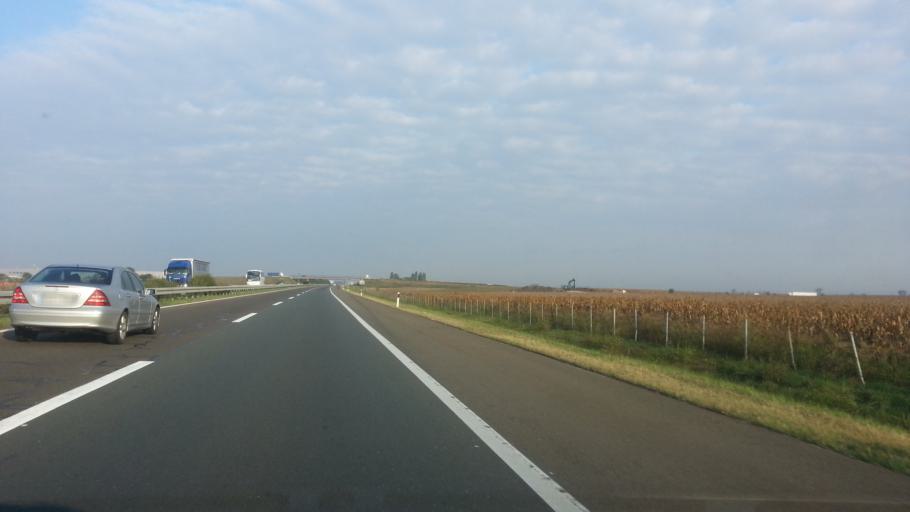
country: RS
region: Autonomna Pokrajina Vojvodina
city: Nova Pazova
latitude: 44.9644
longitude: 20.2439
